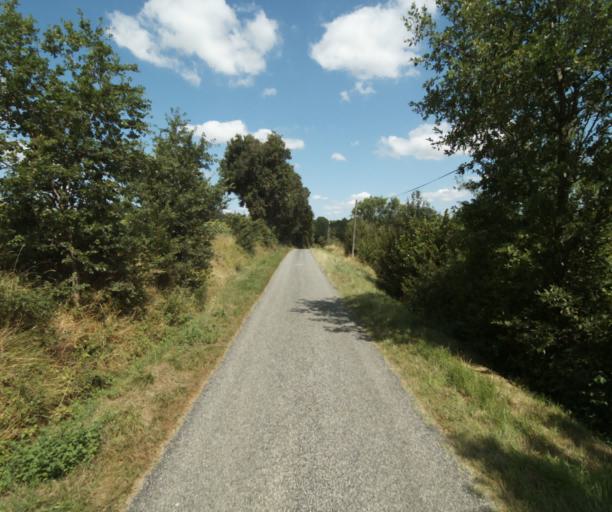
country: FR
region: Midi-Pyrenees
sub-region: Departement de la Haute-Garonne
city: Auriac-sur-Vendinelle
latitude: 43.4783
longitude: 1.7964
